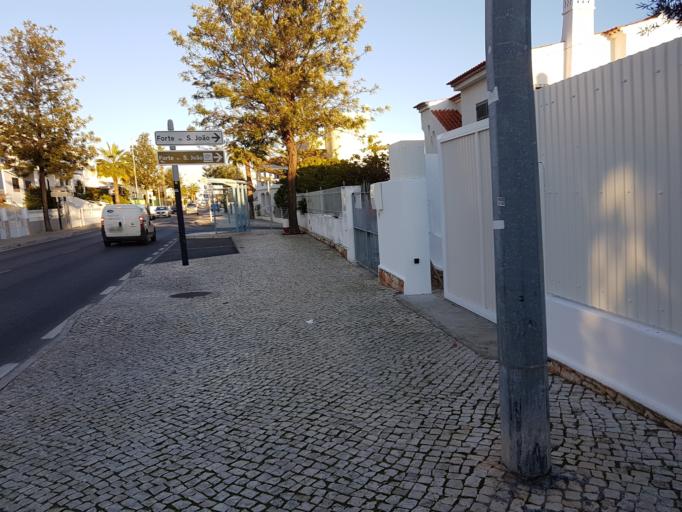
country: PT
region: Faro
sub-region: Albufeira
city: Albufeira
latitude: 37.0874
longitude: -8.2376
